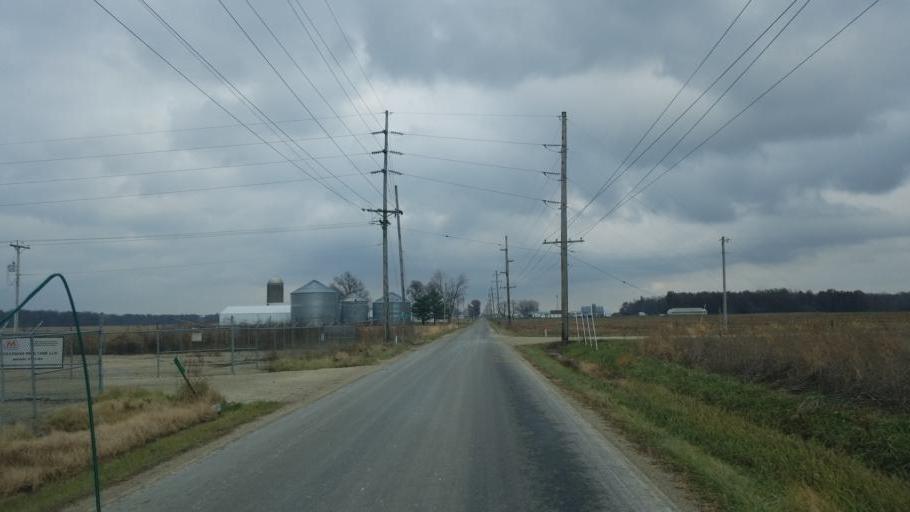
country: US
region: Indiana
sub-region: Adams County
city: Geneva
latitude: 40.5123
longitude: -84.9536
